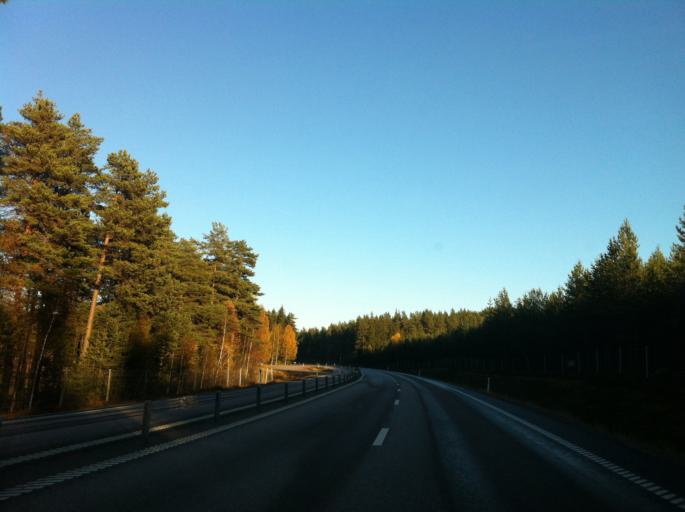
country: SE
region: Dalarna
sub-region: Hedemora Kommun
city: Langshyttan
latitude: 60.5655
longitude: 15.9444
